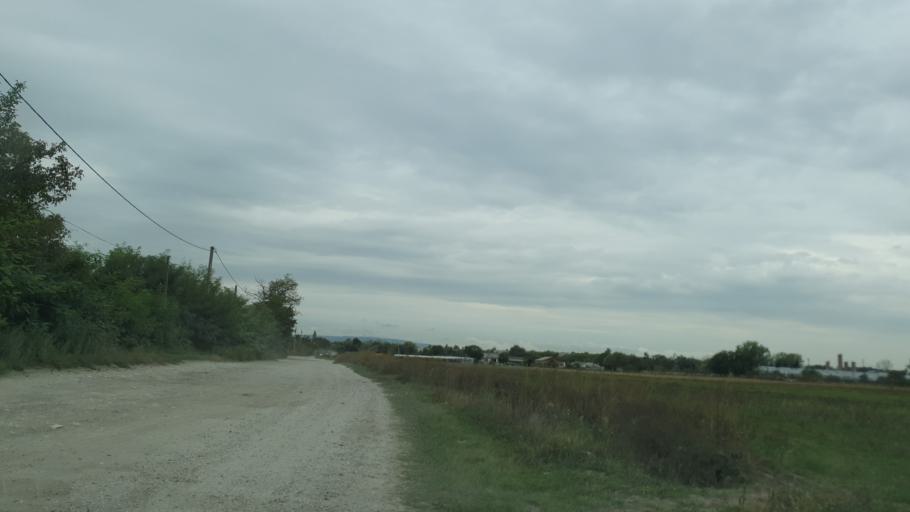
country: HU
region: Budapest
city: Budapest XXI. keruelet
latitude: 47.3991
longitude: 19.0627
